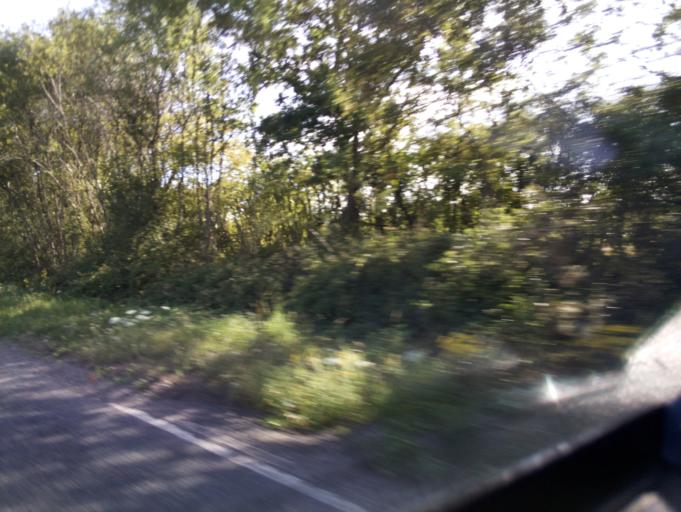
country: GB
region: England
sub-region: Hampshire
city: Romsey
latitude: 50.9689
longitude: -1.5223
